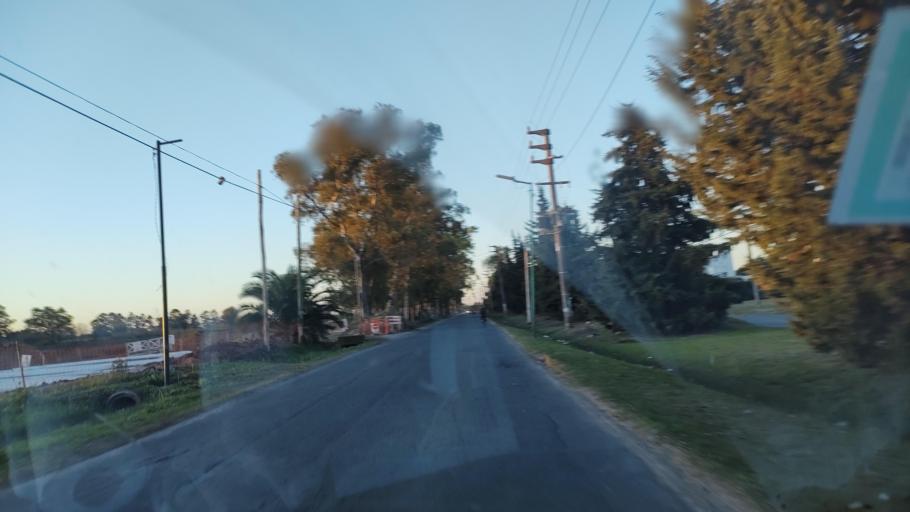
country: AR
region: Buenos Aires
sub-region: Partido de La Plata
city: La Plata
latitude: -34.9043
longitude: -58.0317
